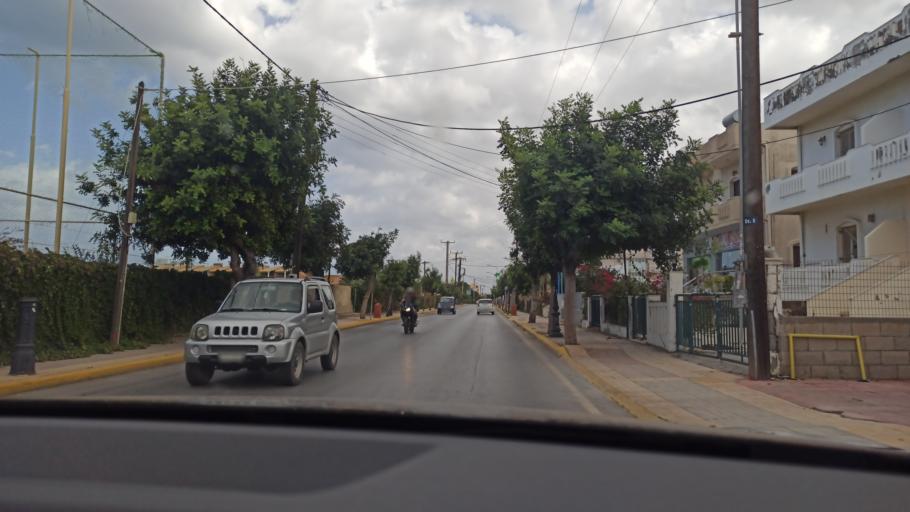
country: GR
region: Crete
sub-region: Nomos Irakleiou
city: Gazi
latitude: 35.3357
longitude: 25.0819
